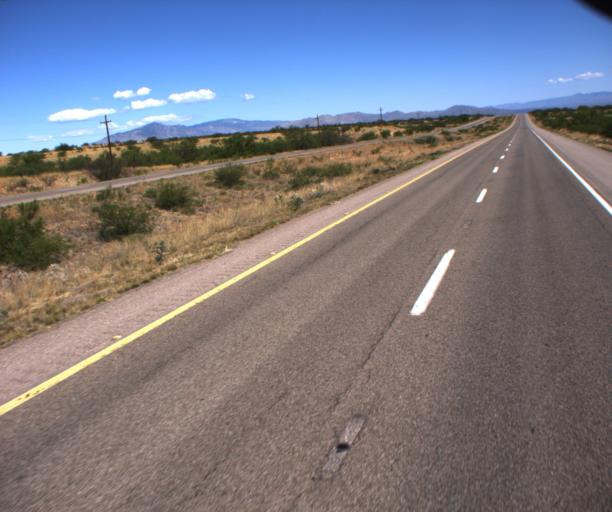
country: US
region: Arizona
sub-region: Cochise County
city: Whetstone
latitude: 31.8835
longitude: -110.3410
